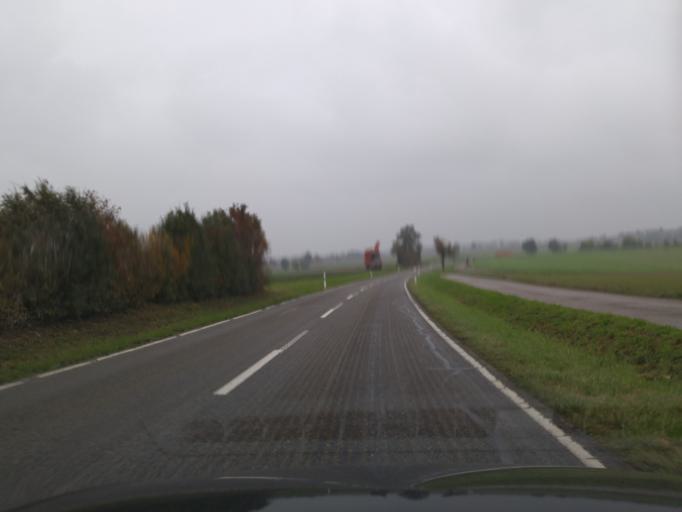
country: DE
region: Baden-Wuerttemberg
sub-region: Regierungsbezirk Stuttgart
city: Bad Wimpfen
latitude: 49.2093
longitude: 9.1484
